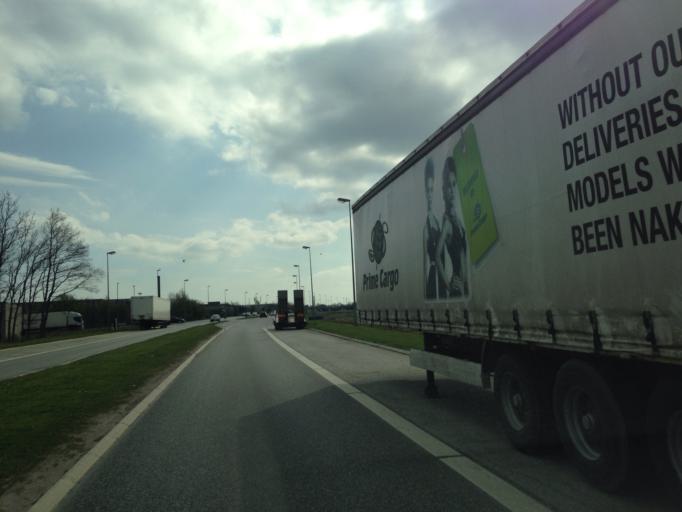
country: DK
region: Capital Region
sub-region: Ishoj Kommune
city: Ishoj
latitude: 55.6191
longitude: 12.3180
